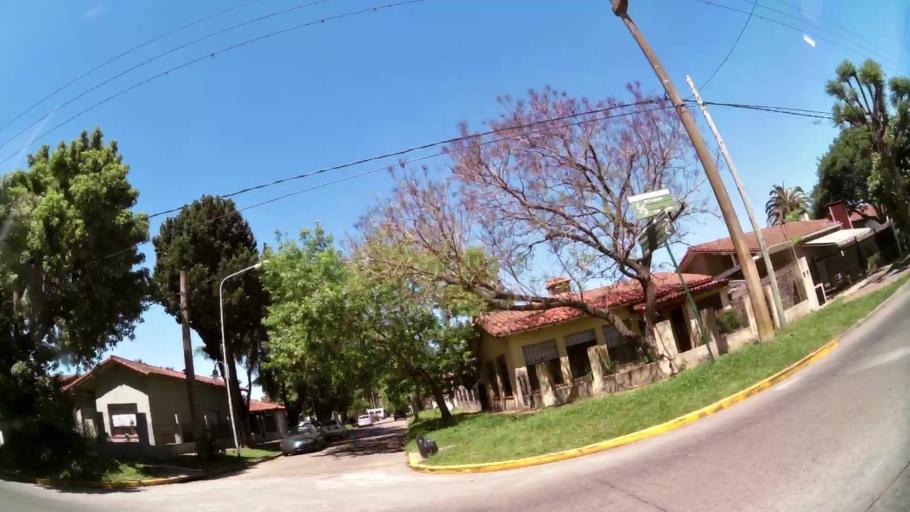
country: AR
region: Buenos Aires
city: Hurlingham
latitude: -34.4924
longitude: -58.6537
